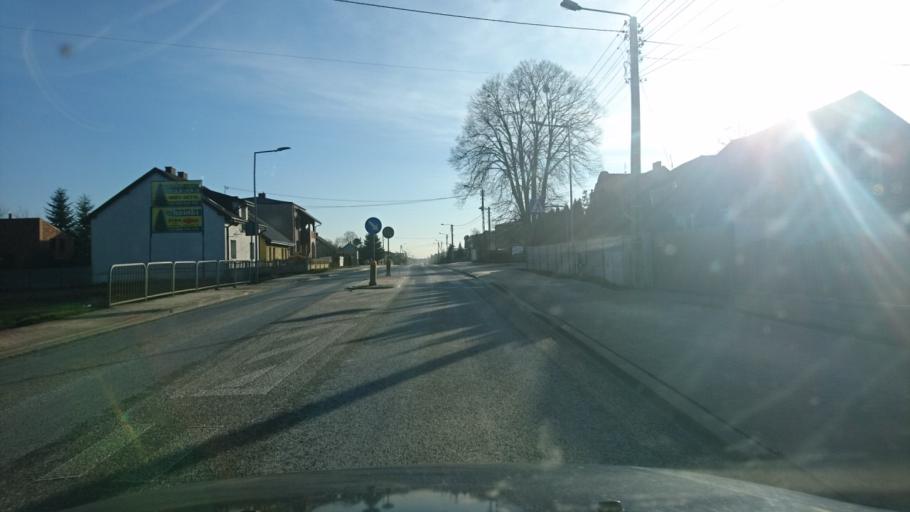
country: PL
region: Silesian Voivodeship
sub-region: Powiat klobucki
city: Starokrzepice
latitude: 51.0154
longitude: 18.6542
